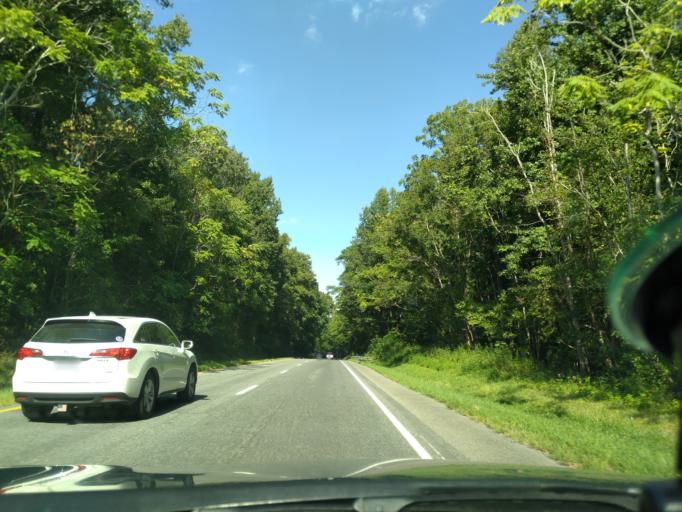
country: US
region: Virginia
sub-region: King George County
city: King George
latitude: 38.1553
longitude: -77.2088
